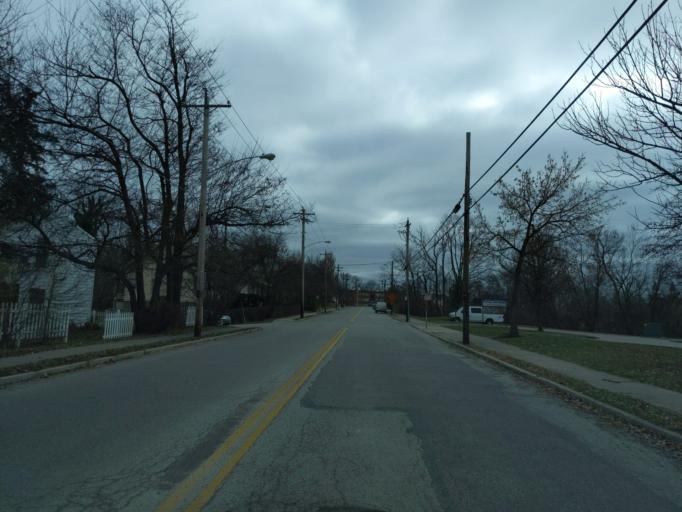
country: US
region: Ohio
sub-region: Hamilton County
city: North College Hill
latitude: 39.1922
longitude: -84.5480
